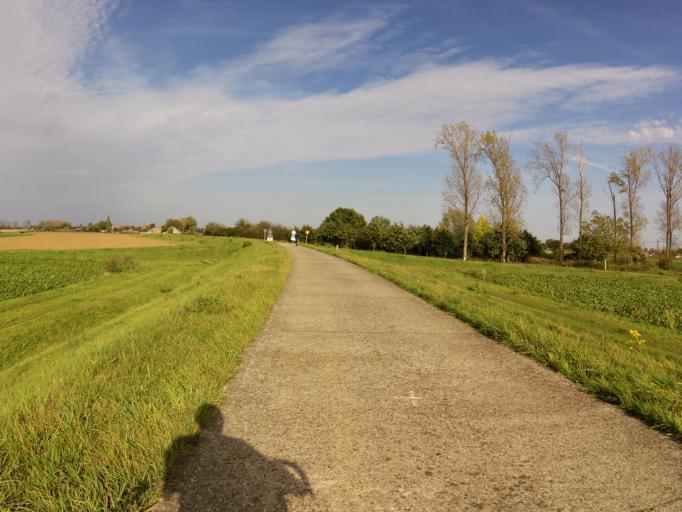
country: BE
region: Flanders
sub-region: Provincie Limburg
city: Maaseik
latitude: 51.0674
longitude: 5.7891
